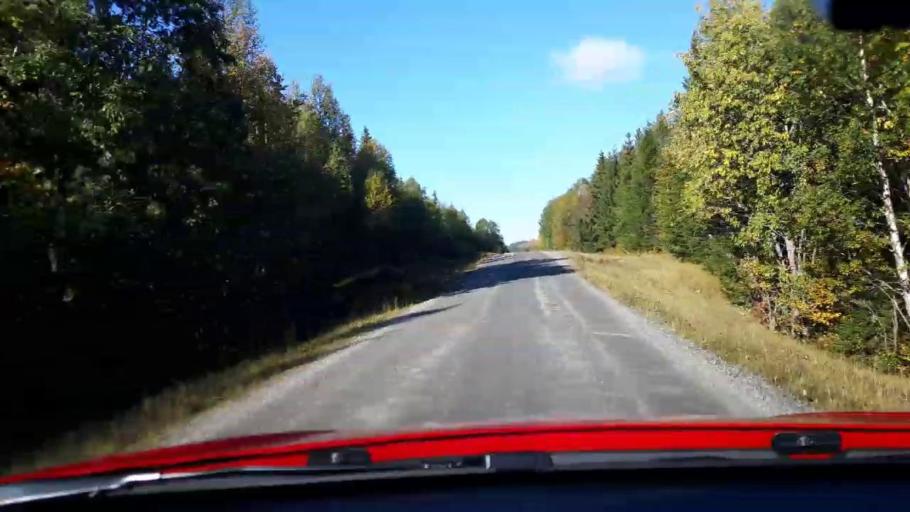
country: NO
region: Nord-Trondelag
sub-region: Lierne
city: Sandvika
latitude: 64.5865
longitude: 13.8765
